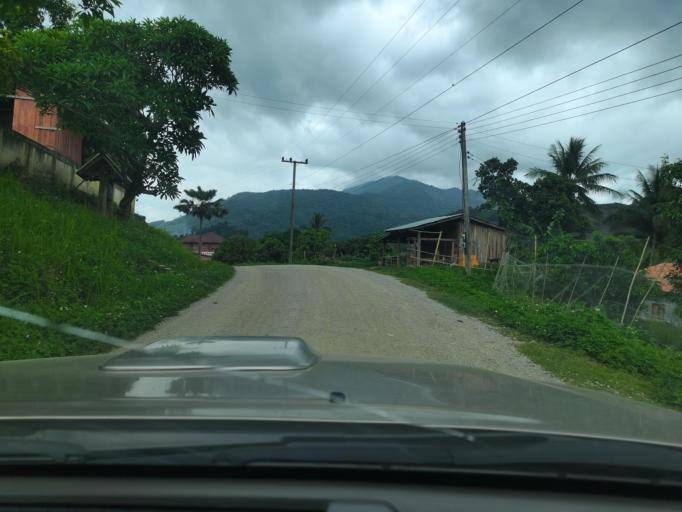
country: TH
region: Phayao
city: Phu Sang
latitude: 19.6875
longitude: 100.5018
